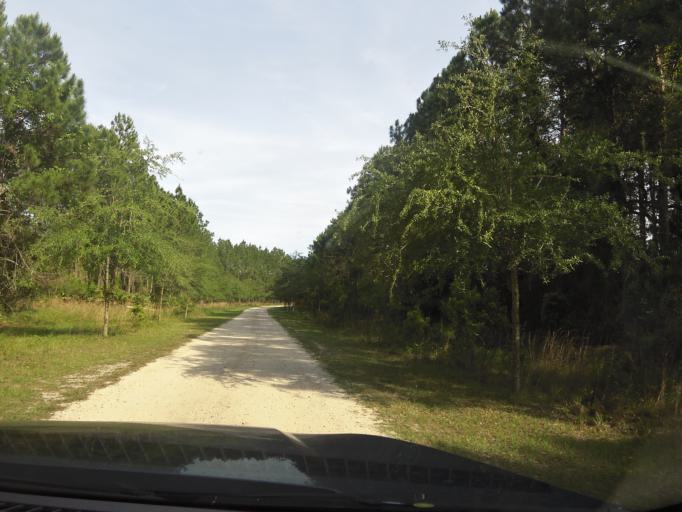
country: US
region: Florida
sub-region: Nassau County
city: Fernandina Beach
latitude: 30.4955
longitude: -81.4920
